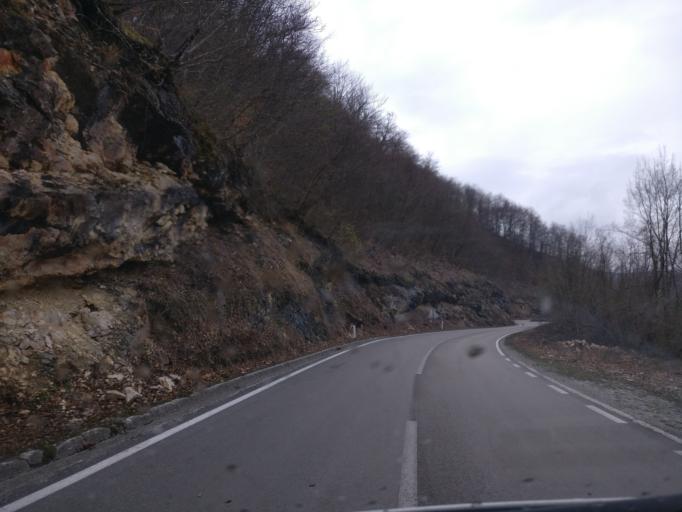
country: ME
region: Opstina Pluzine
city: Pluzine
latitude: 43.1394
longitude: 18.8298
